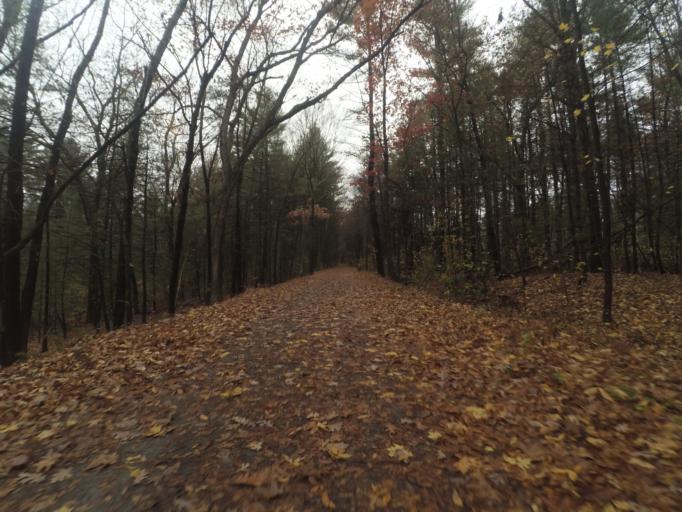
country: US
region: Massachusetts
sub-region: Middlesex County
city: Bedford
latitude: 42.5175
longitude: -71.2795
